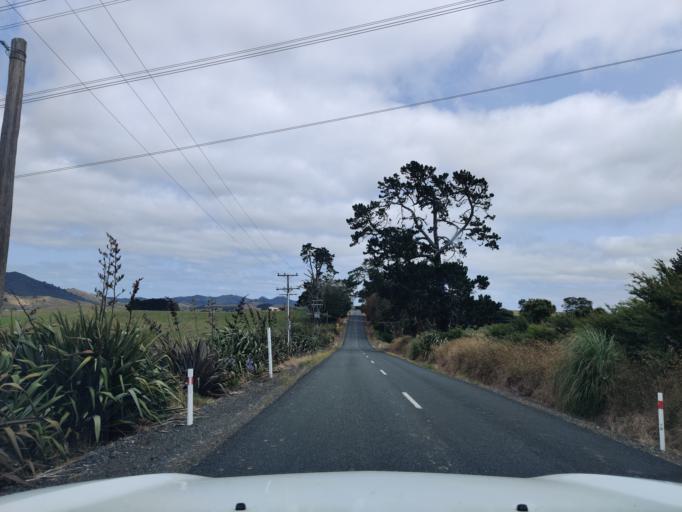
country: NZ
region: Waikato
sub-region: Waikato District
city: Te Kauwhata
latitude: -37.5163
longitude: 175.1764
